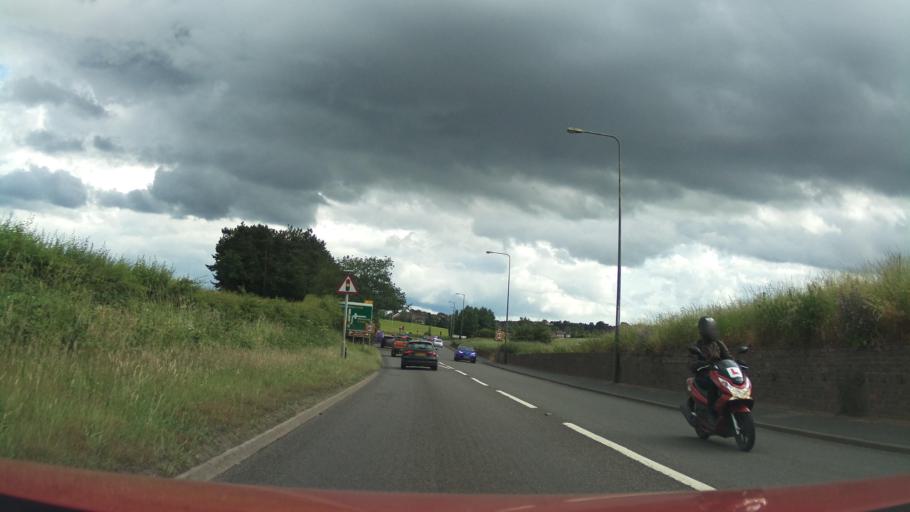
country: GB
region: England
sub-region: Worcestershire
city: Kidderminster
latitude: 52.4088
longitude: -2.2269
